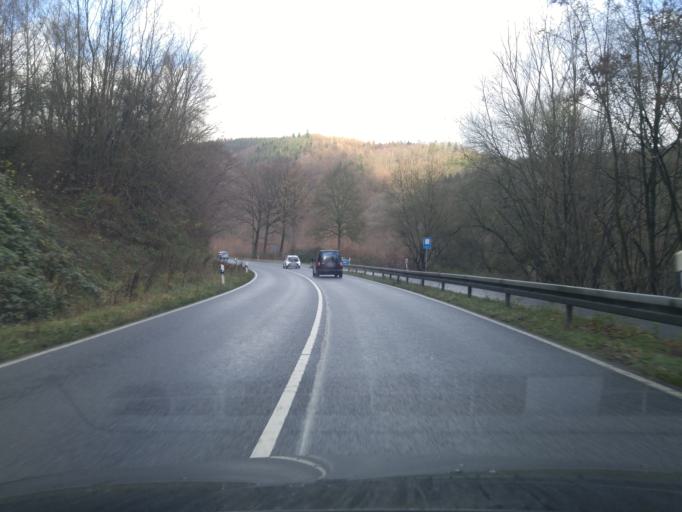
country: DE
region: Lower Saxony
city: Buhren
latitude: 51.4658
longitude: 9.6399
